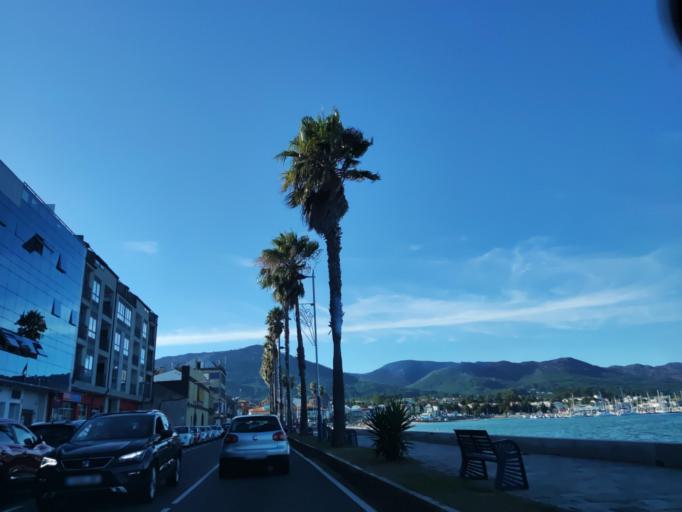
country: ES
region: Galicia
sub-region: Provincia da Coruna
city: Boiro
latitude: 42.6001
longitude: -8.9349
